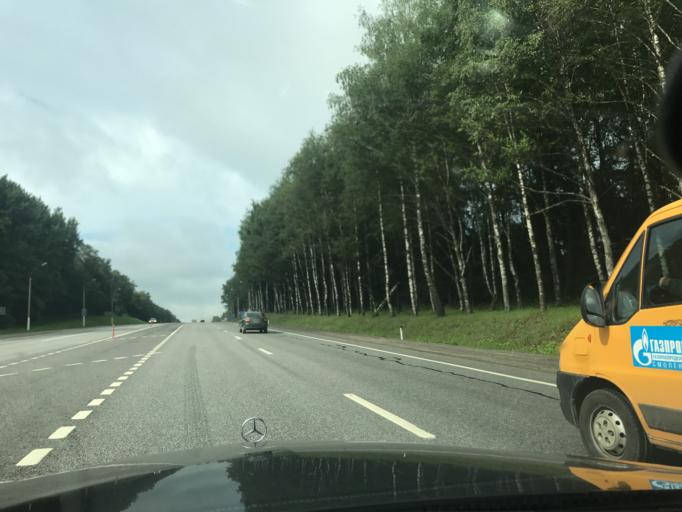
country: RU
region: Smolensk
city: Kardymovo
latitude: 55.0116
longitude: 32.2916
